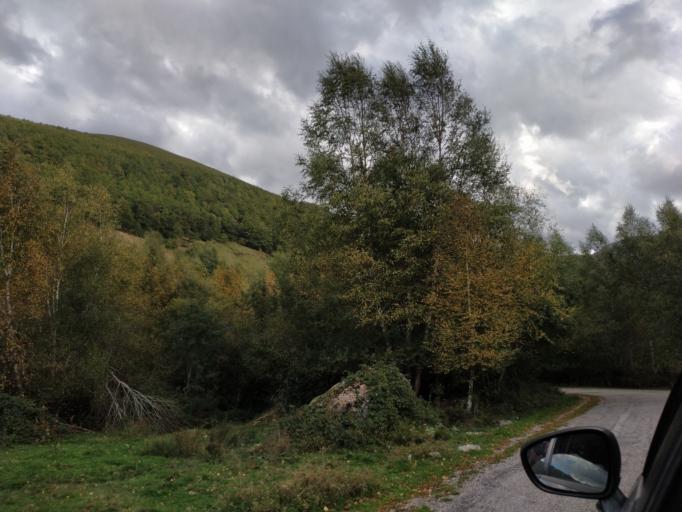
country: ES
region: Castille and Leon
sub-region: Provincia de Leon
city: Candin
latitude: 42.8606
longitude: -6.8558
